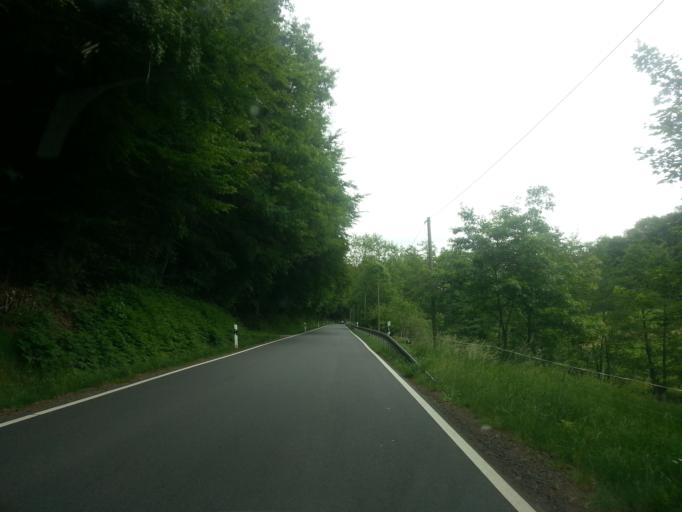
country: DE
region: Hesse
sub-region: Regierungsbezirk Darmstadt
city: Seeheim-Jugenheim
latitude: 49.7313
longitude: 8.6726
